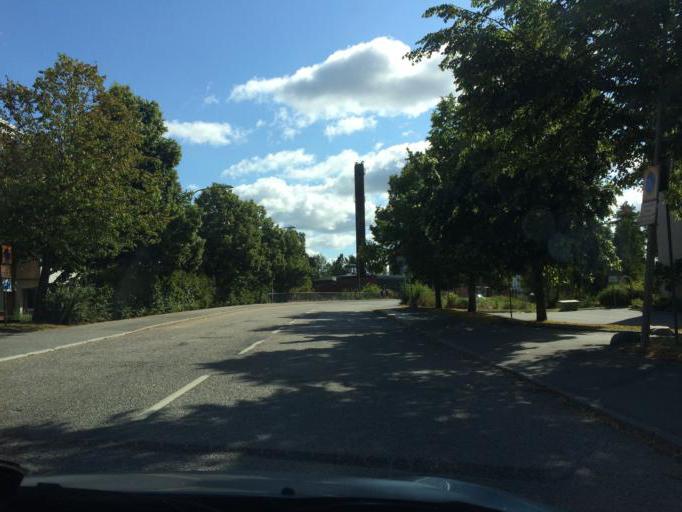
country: SE
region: Stockholm
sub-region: Nacka Kommun
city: Nacka
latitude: 59.2795
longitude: 18.1368
